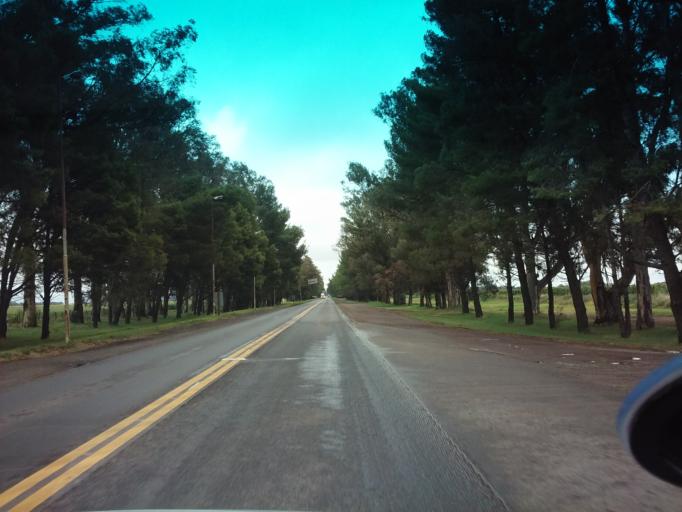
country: AR
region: La Pampa
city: Catrilo
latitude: -36.4108
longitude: -63.3881
